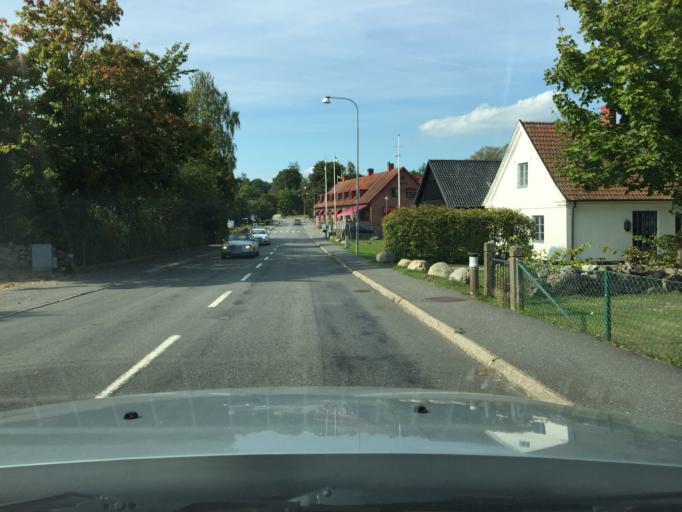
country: SE
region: Skane
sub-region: Kristianstads Kommun
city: Degeberga
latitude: 55.7249
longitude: 14.1051
